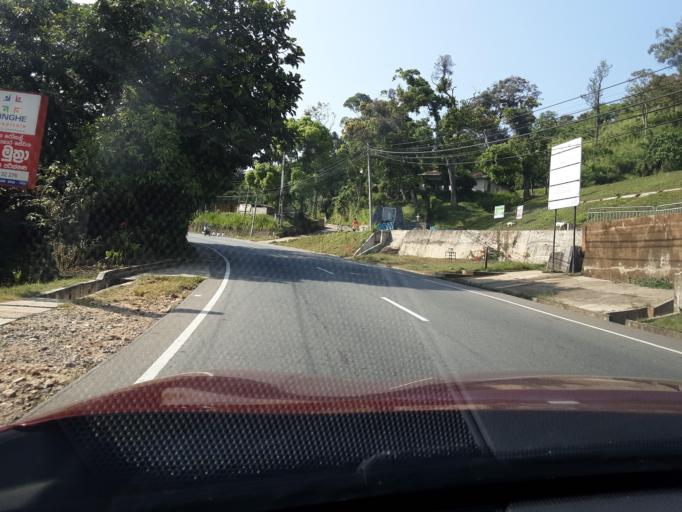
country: LK
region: Uva
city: Badulla
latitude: 6.9792
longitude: 81.0819
